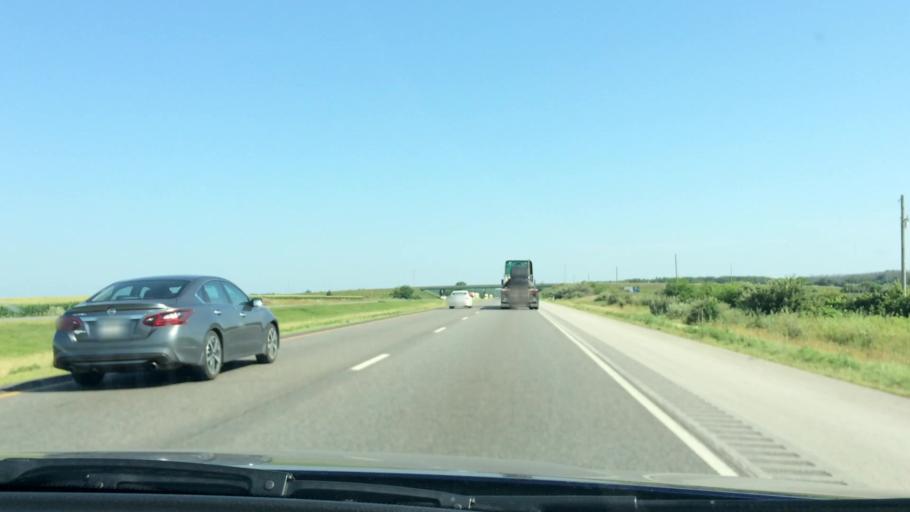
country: US
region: Indiana
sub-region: Jasper County
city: Rensselaer
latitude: 40.8845
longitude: -87.1988
